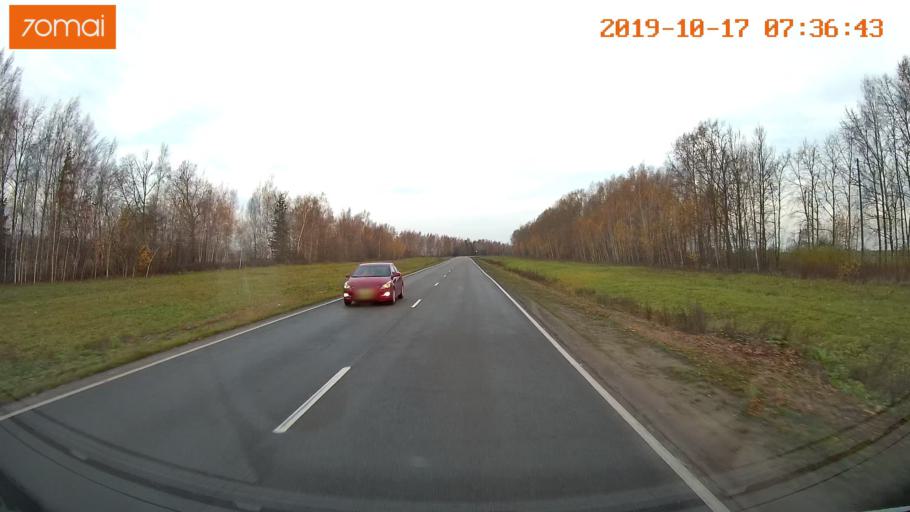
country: RU
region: Ivanovo
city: Gavrilov Posad
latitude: 56.4423
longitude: 39.9124
